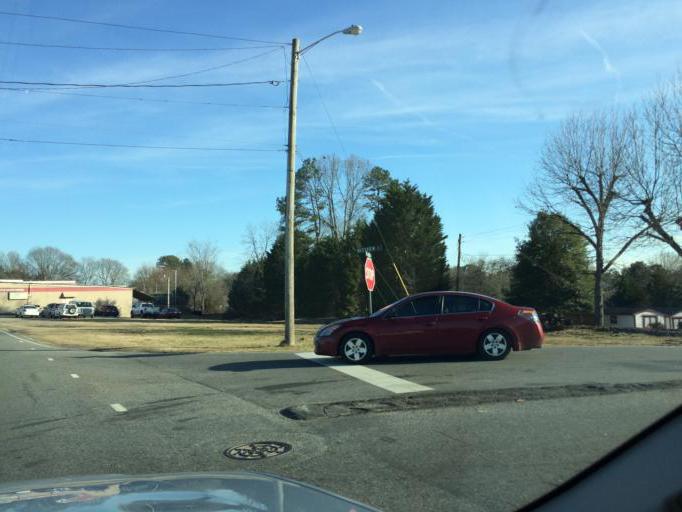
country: US
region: North Carolina
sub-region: Rutherford County
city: Forest City
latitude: 35.3403
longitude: -81.8786
